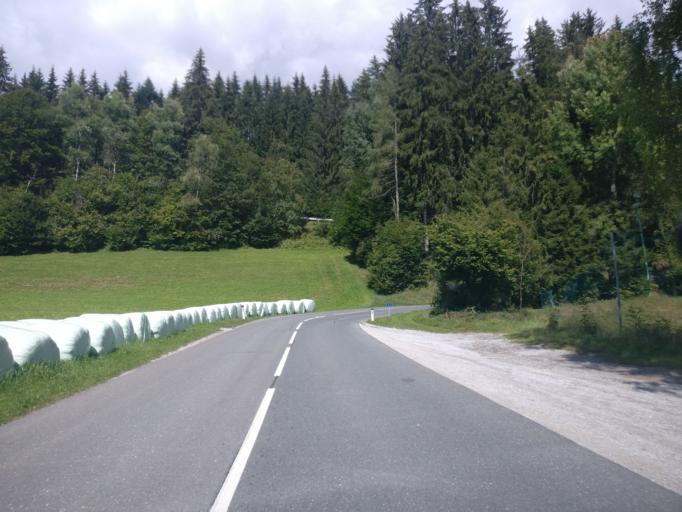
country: AT
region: Salzburg
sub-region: Politischer Bezirk Sankt Johann im Pongau
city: Muhlbach am Hochkonig
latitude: 47.3787
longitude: 13.1313
